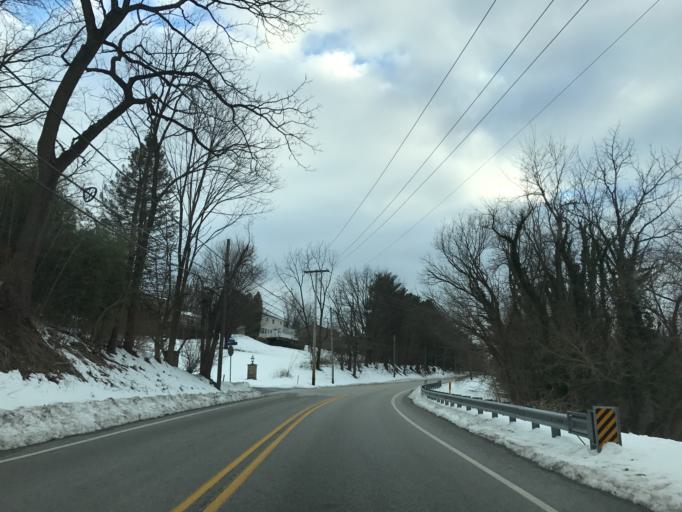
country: US
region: Pennsylvania
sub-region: York County
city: Grantley
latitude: 39.9288
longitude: -76.7113
